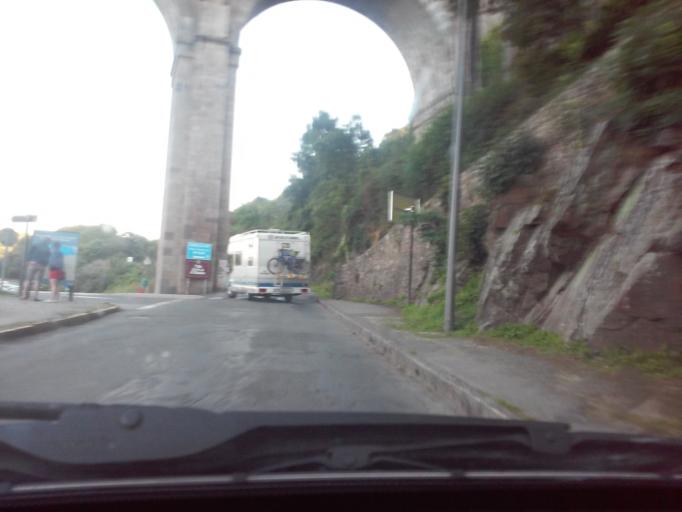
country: FR
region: Brittany
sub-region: Departement des Cotes-d'Armor
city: Dinan
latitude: 48.4549
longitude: -2.0391
